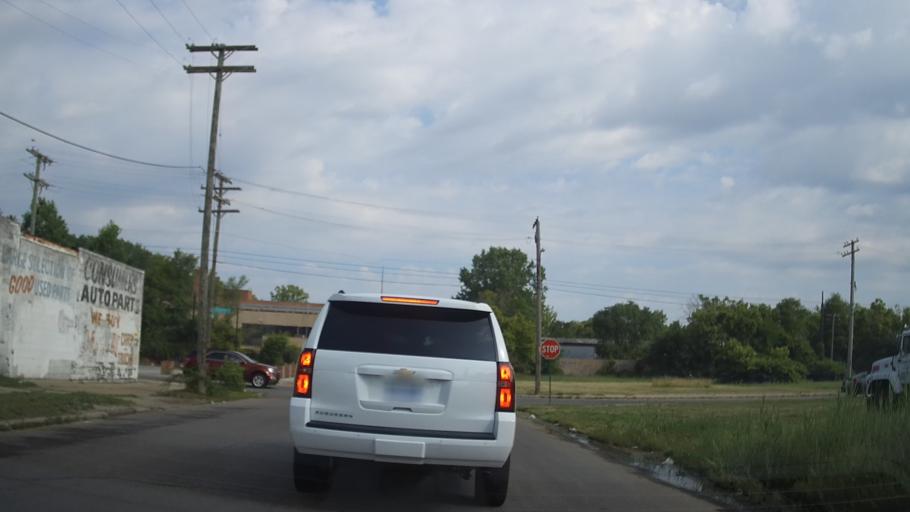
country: US
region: Michigan
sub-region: Wayne County
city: Detroit
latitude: 42.3482
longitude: -83.0081
